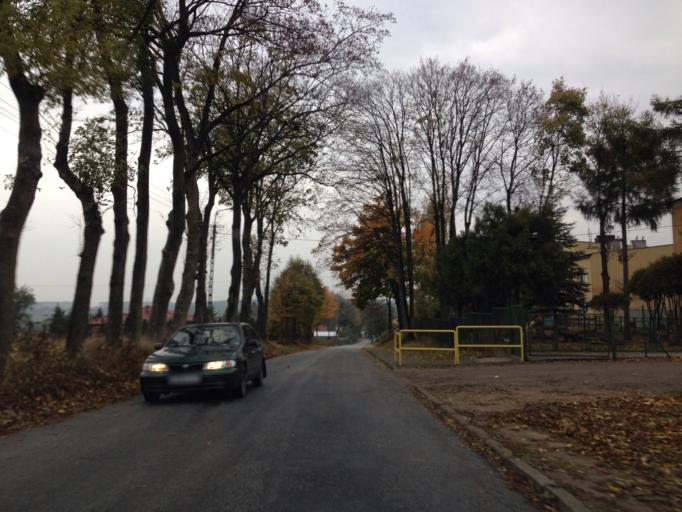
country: PL
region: Kujawsko-Pomorskie
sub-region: Powiat rypinski
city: Rypin
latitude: 53.1212
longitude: 19.3891
